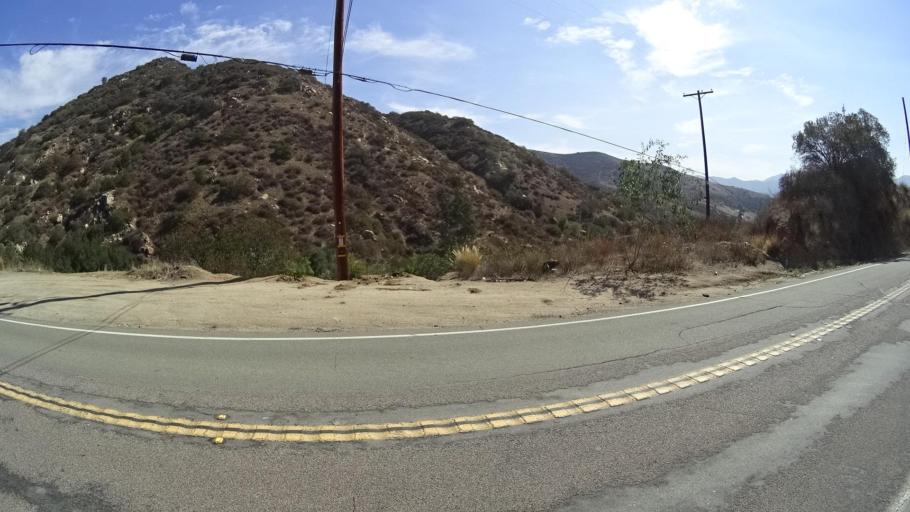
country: US
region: California
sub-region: San Diego County
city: Harbison Canyon
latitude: 32.8099
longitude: -116.8439
